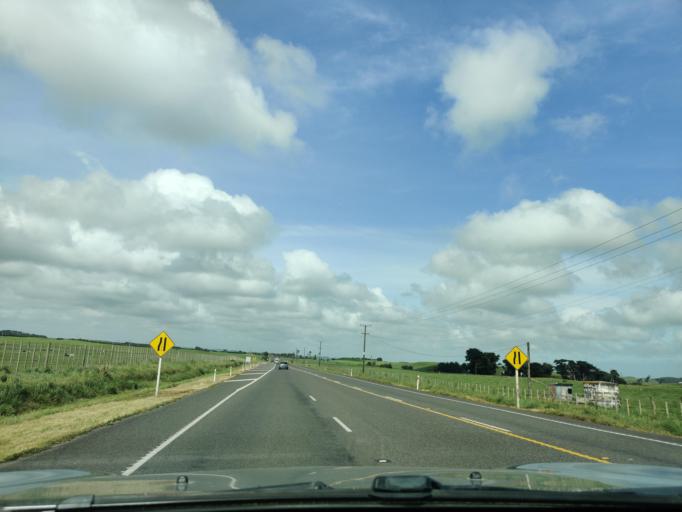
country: NZ
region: Taranaki
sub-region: South Taranaki District
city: Patea
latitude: -39.7687
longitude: 174.6580
